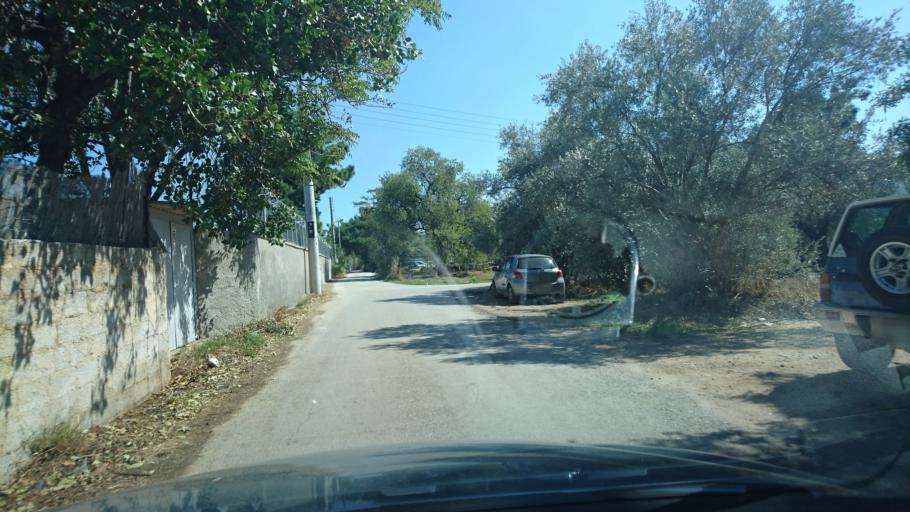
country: GR
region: Attica
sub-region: Nomarchia Athinas
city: Khalandrion
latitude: 38.0170
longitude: 23.8111
